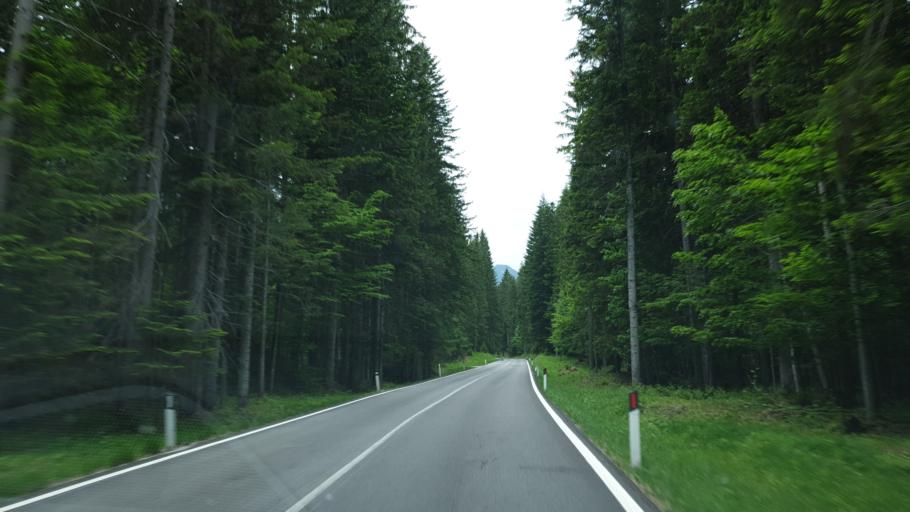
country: IT
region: Veneto
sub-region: Provincia di Belluno
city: San Vito
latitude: 46.5313
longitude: 12.2794
